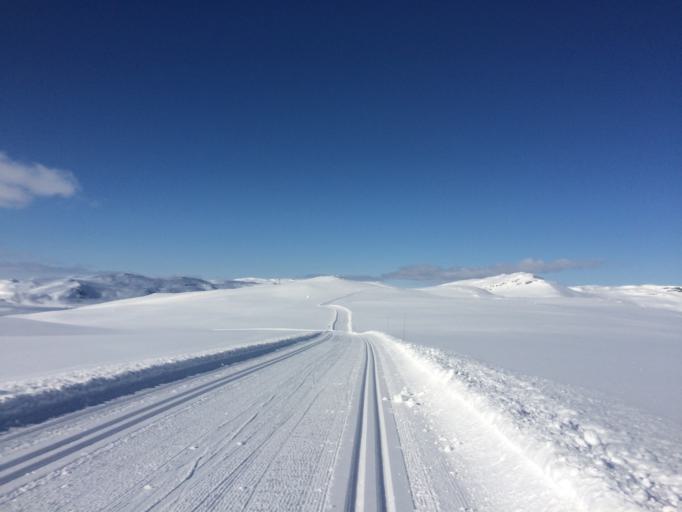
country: NO
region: Oppland
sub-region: Ringebu
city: Ringebu
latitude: 61.3574
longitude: 10.0856
